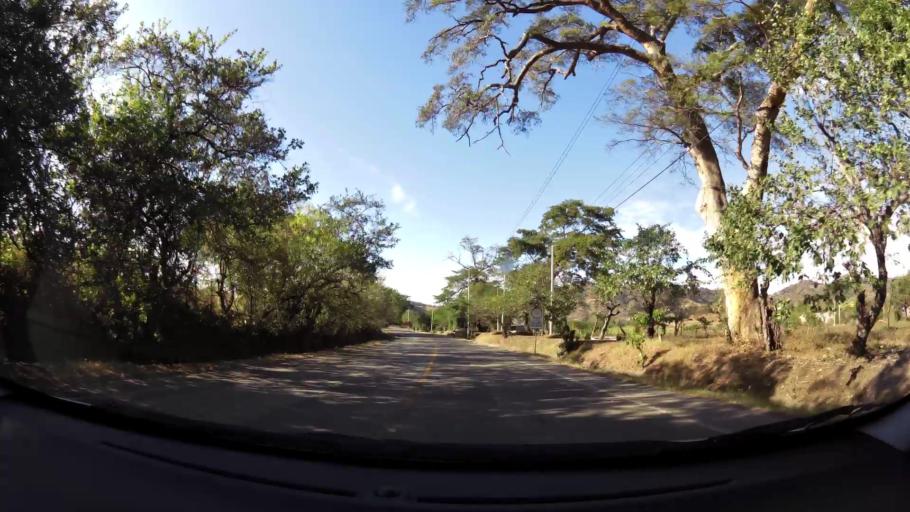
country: SV
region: Santa Ana
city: Texistepeque
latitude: 14.1289
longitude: -89.5006
